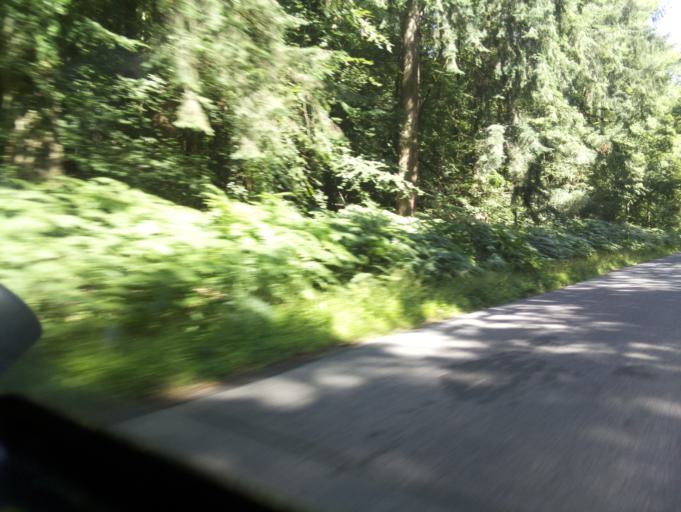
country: GB
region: England
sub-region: Gloucestershire
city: Cinderford
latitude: 51.7808
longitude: -2.5002
